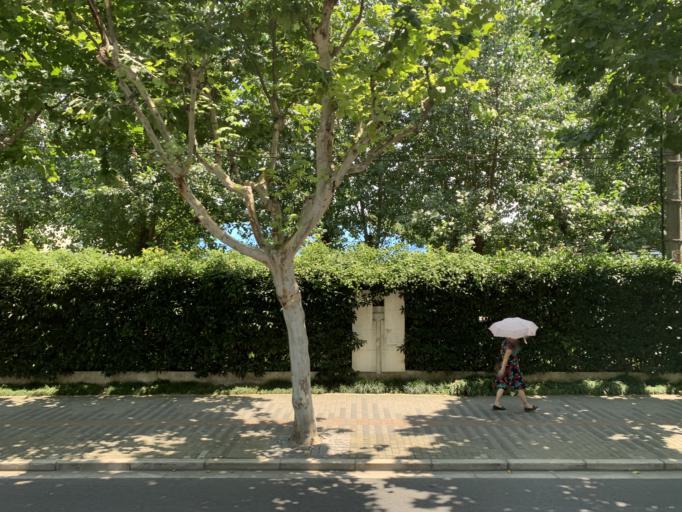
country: CN
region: Shanghai Shi
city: Pudong
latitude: 31.2468
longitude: 121.5618
